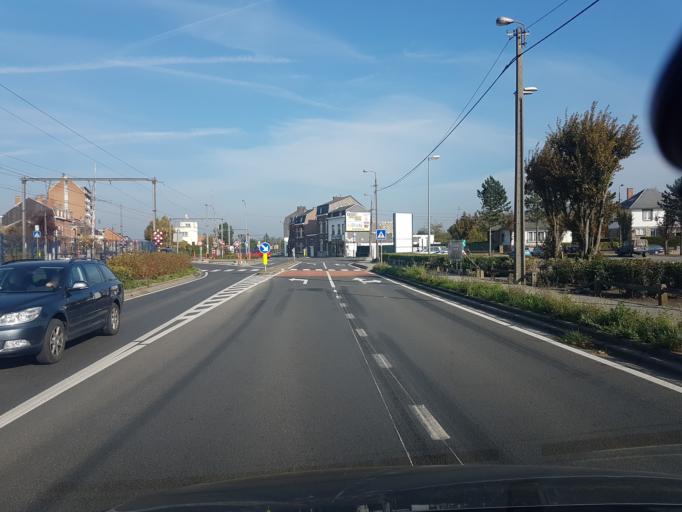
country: BE
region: Wallonia
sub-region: Province de Namur
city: Namur
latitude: 50.4426
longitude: 4.8676
